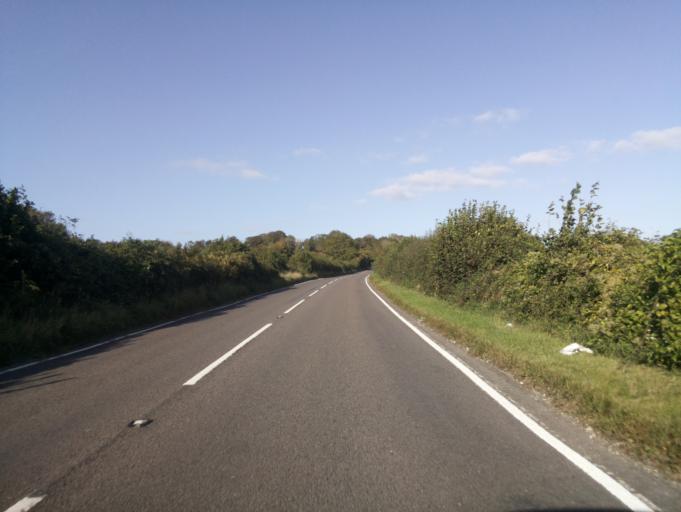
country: GB
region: England
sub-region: Hampshire
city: Four Marks
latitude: 51.0377
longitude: -1.0700
